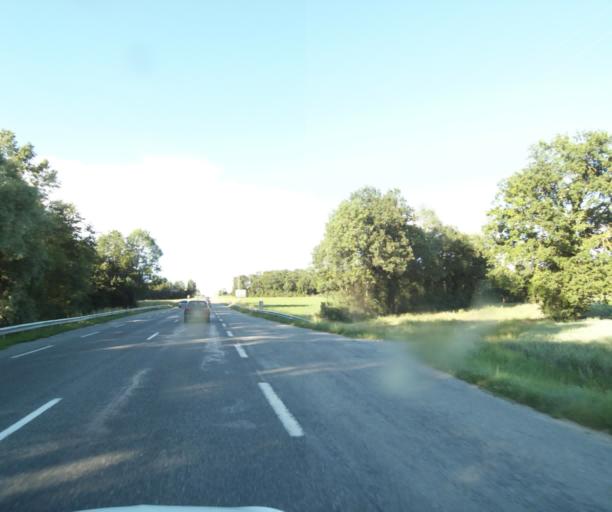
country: FR
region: Rhone-Alpes
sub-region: Departement de la Haute-Savoie
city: Veigy-Foncenex
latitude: 46.2917
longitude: 6.2724
